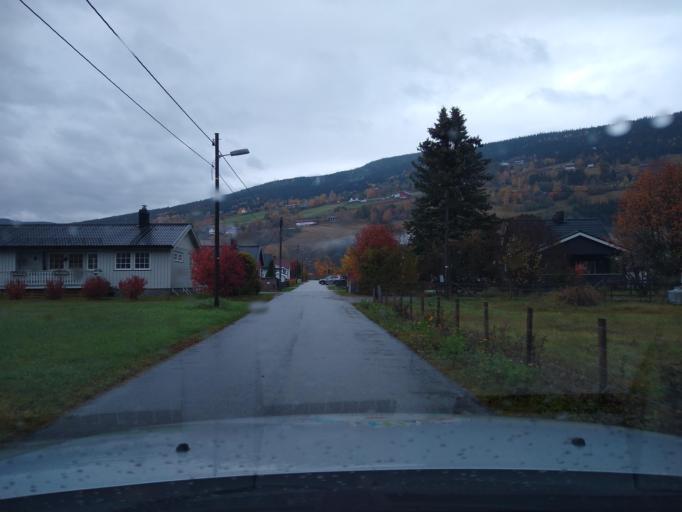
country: NO
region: Oppland
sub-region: Ringebu
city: Ringebu
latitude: 61.5224
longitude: 10.1475
